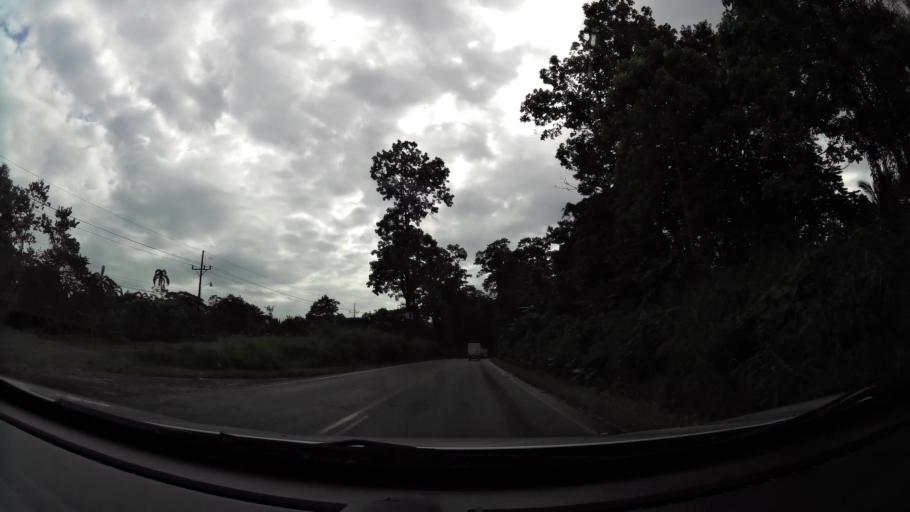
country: CR
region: Limon
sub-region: Canton de Siquirres
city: Siquirres
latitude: 10.1133
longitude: -83.5398
